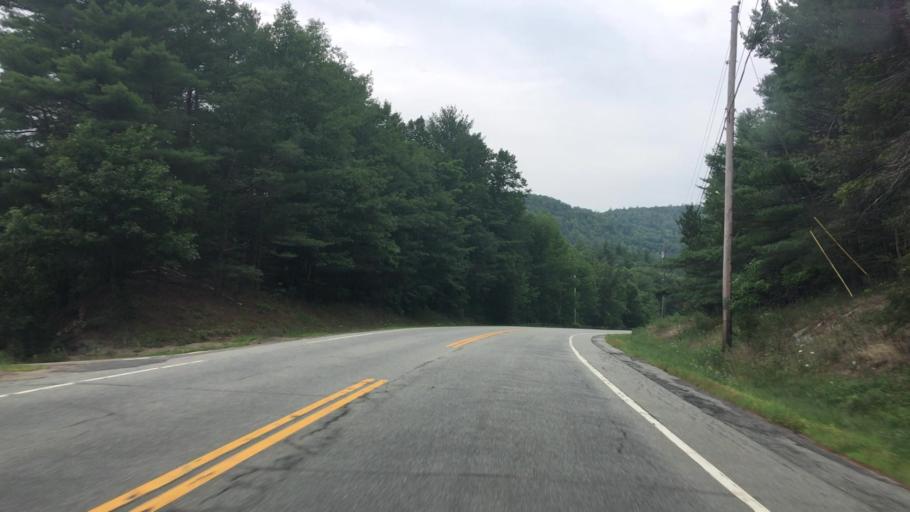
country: US
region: New York
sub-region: Essex County
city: Lake Placid
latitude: 44.3127
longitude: -73.7856
